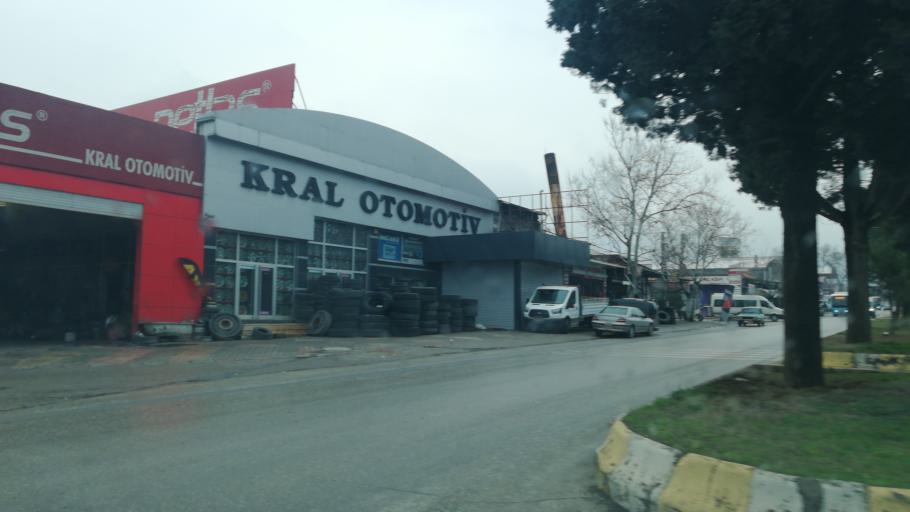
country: TR
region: Kahramanmaras
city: Kahramanmaras
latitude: 37.5640
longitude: 36.9598
